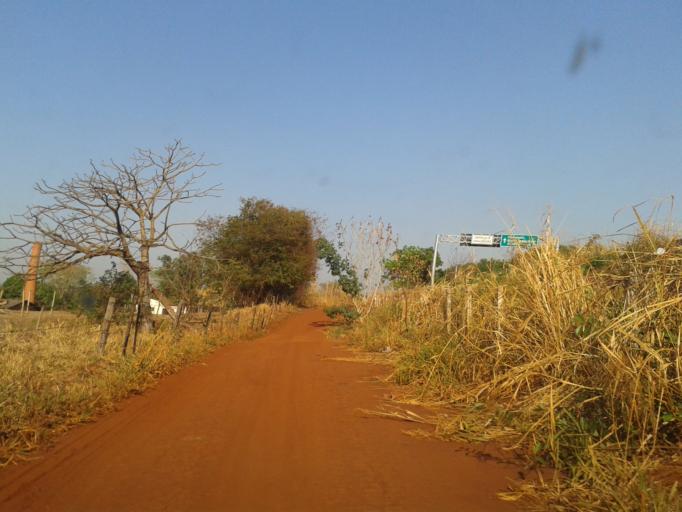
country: BR
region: Minas Gerais
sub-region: Ituiutaba
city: Ituiutaba
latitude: -18.9646
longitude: -49.4799
